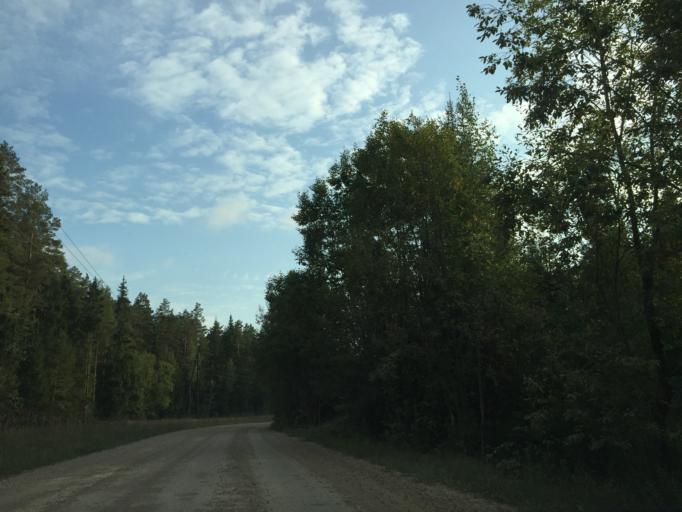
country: LV
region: Ikskile
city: Ikskile
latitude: 56.8035
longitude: 24.4403
